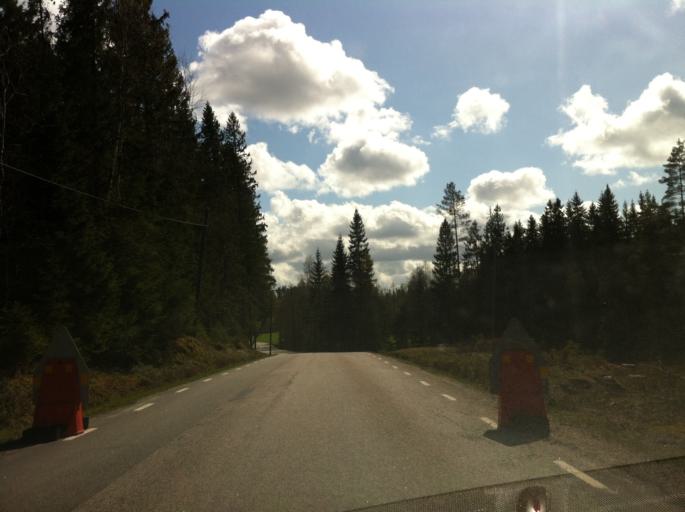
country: SE
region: Vaestra Goetaland
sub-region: Alingsas Kommun
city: Alingsas
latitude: 57.8299
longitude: 12.6471
